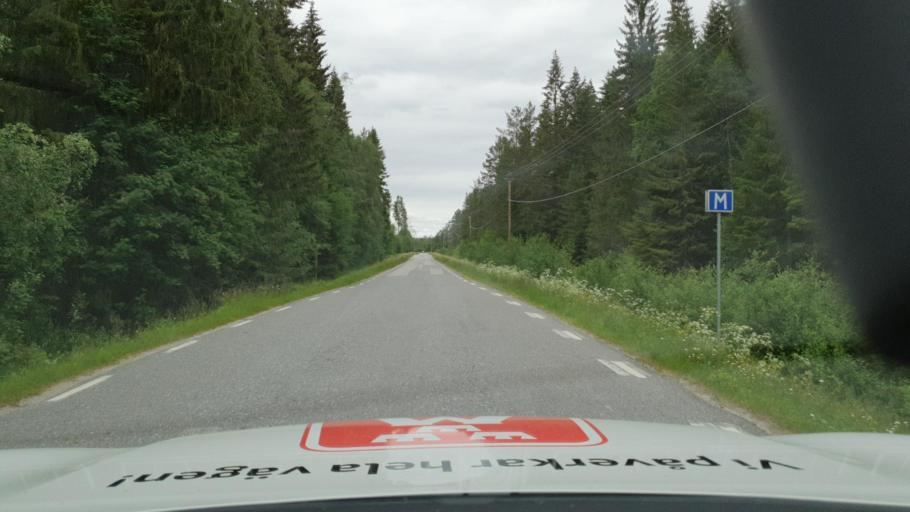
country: SE
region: Vaesterbotten
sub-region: Nordmalings Kommun
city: Nordmaling
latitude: 63.5218
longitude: 19.4183
